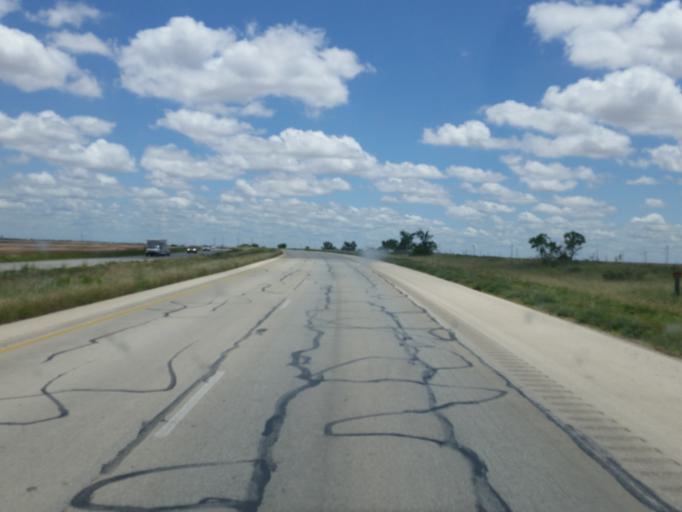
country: US
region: Texas
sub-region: Nolan County
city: Roscoe
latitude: 32.4909
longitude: -100.6330
